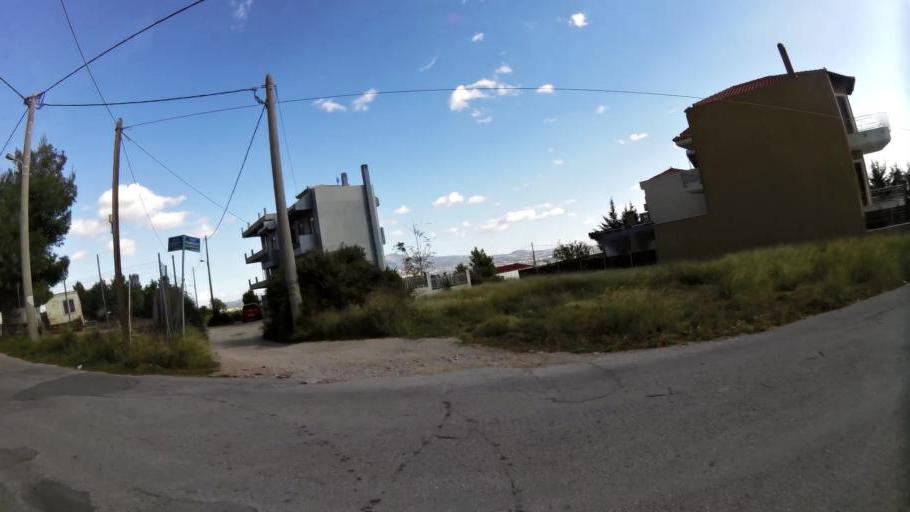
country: GR
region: Attica
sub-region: Nomarchia Anatolikis Attikis
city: Acharnes
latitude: 38.1141
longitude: 23.7232
